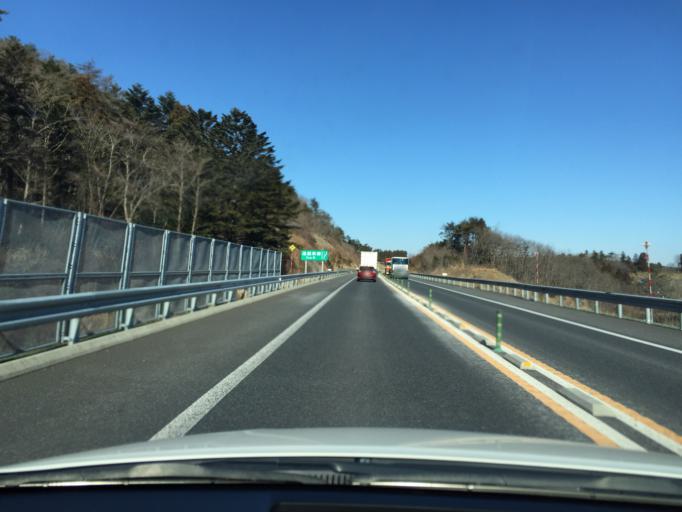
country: JP
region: Miyagi
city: Marumori
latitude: 37.7439
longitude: 140.9051
